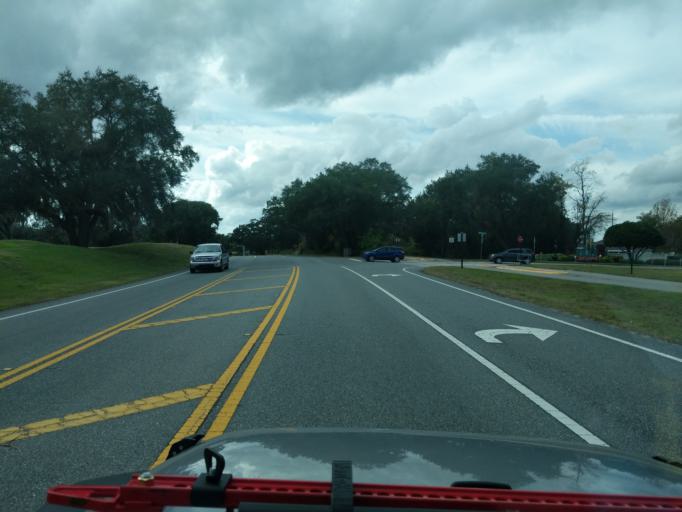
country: US
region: Florida
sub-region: Lake County
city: Groveland
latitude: 28.5667
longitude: -81.8161
